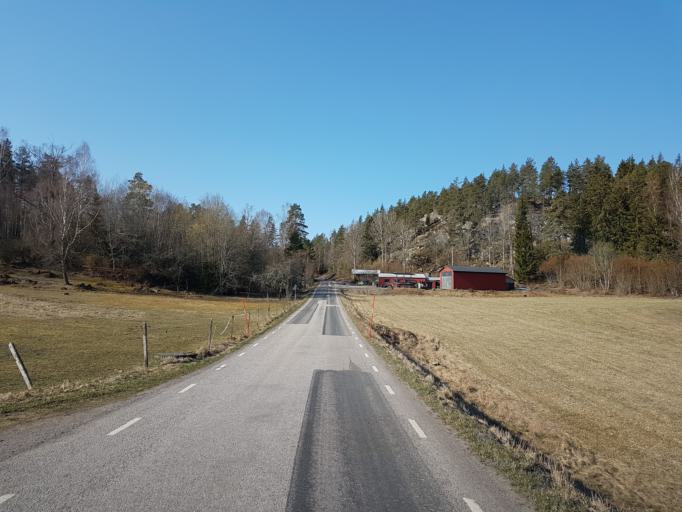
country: SE
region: OEstergoetland
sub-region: Valdemarsviks Kommun
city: Gusum
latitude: 58.1920
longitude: 16.2883
